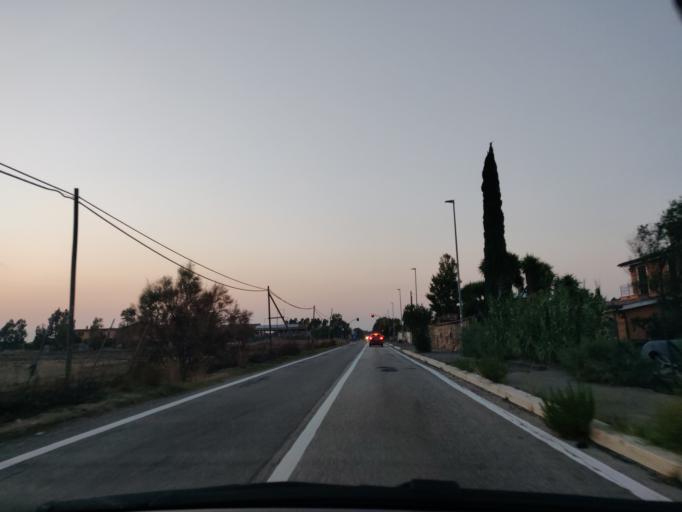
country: IT
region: Latium
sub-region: Citta metropolitana di Roma Capitale
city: Npp 23 (Parco Leonardo)
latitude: 41.8188
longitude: 12.2961
